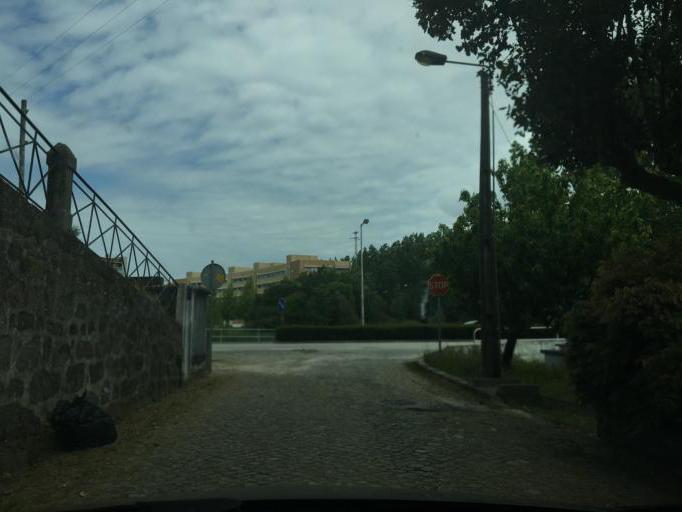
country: PT
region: Porto
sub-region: Maia
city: Anta
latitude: 41.2660
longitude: -8.6123
